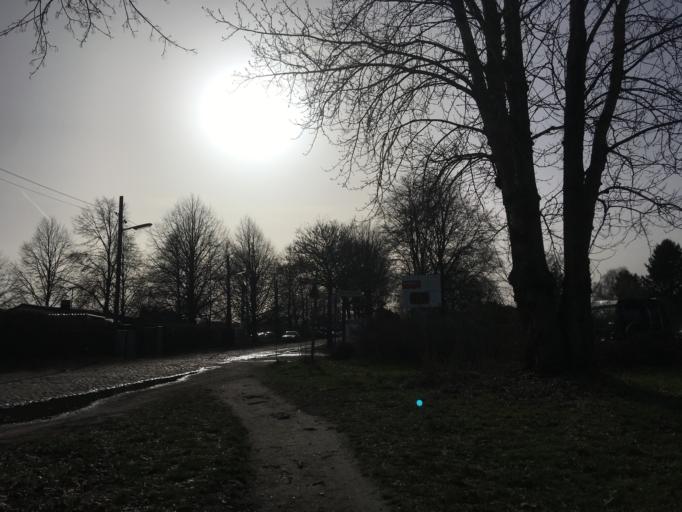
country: DE
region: Berlin
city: Lubars
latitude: 52.6091
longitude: 13.3482
